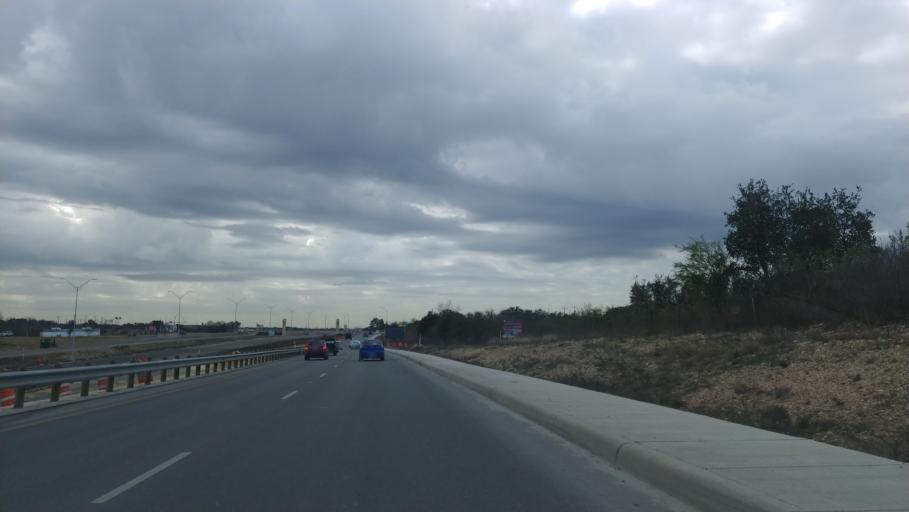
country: US
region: Texas
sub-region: Bexar County
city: Lackland Air Force Base
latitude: 29.4149
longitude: -98.7105
